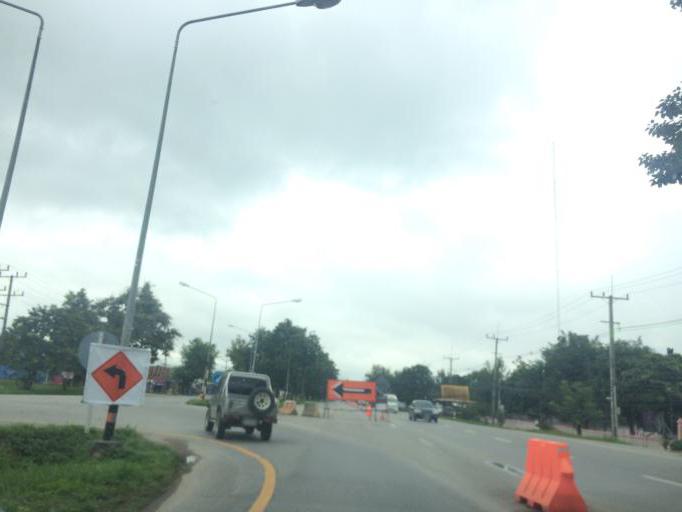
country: TH
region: Chiang Rai
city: Mae Lao
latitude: 19.7569
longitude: 99.7332
